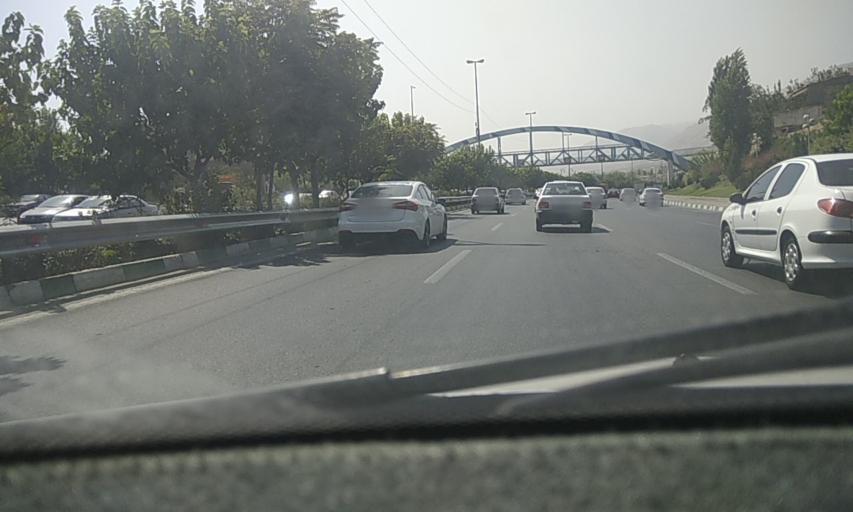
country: IR
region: Tehran
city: Tehran
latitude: 35.7541
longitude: 51.2746
